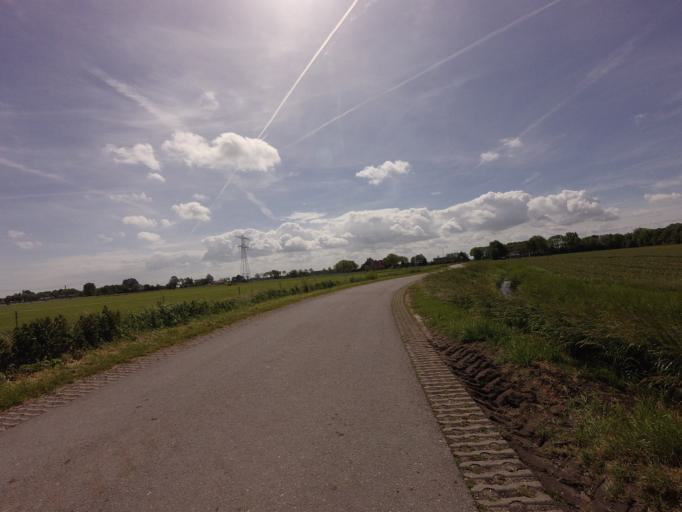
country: NL
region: North Holland
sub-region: Gemeente Opmeer
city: Opmeer
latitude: 52.6545
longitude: 4.9883
